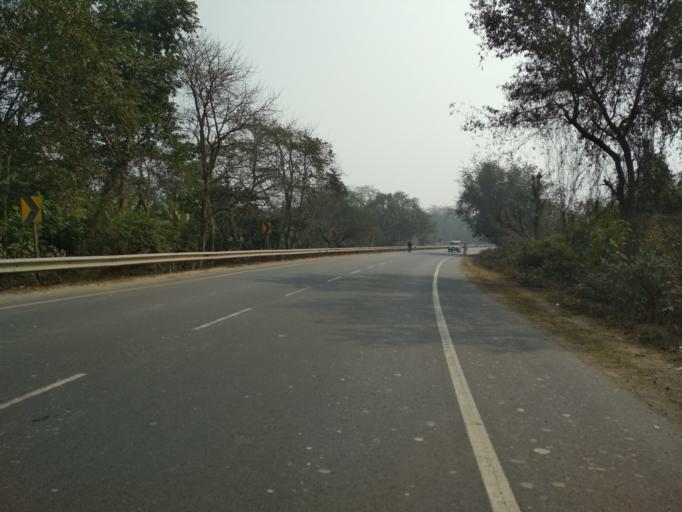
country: IN
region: Bihar
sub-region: Khagaria
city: Khagaria
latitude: 25.5054
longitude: 86.5884
